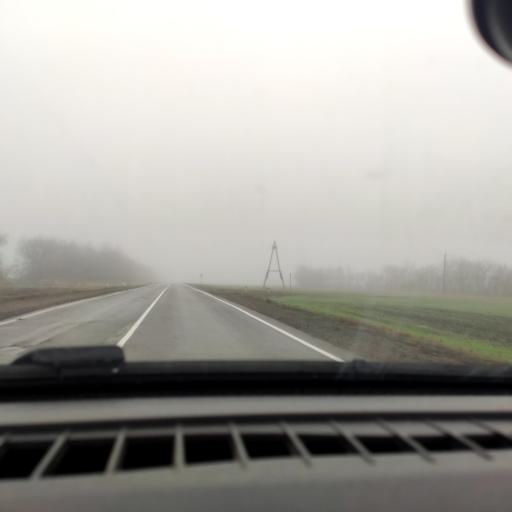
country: RU
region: Voronezj
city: Ostrogozhsk
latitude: 50.7901
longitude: 38.9343
